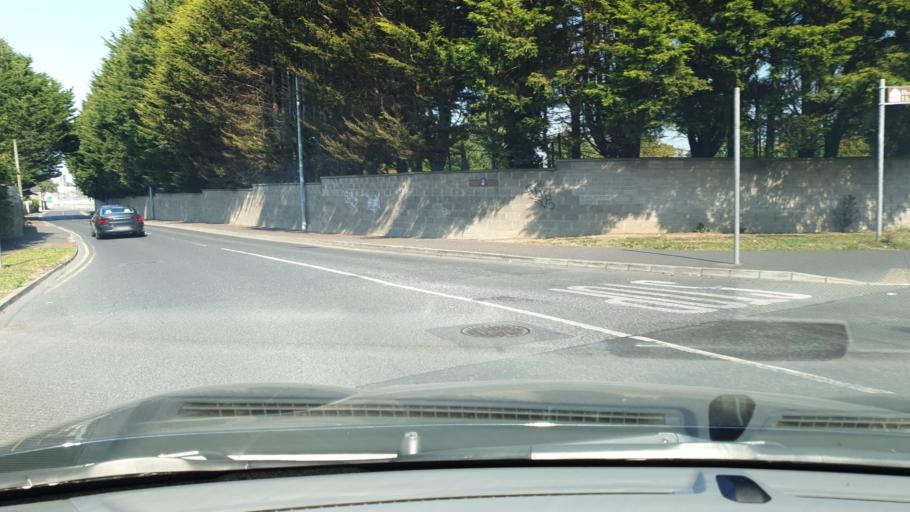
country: IE
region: Leinster
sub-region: An Mhi
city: Navan
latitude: 53.6461
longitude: -6.6931
